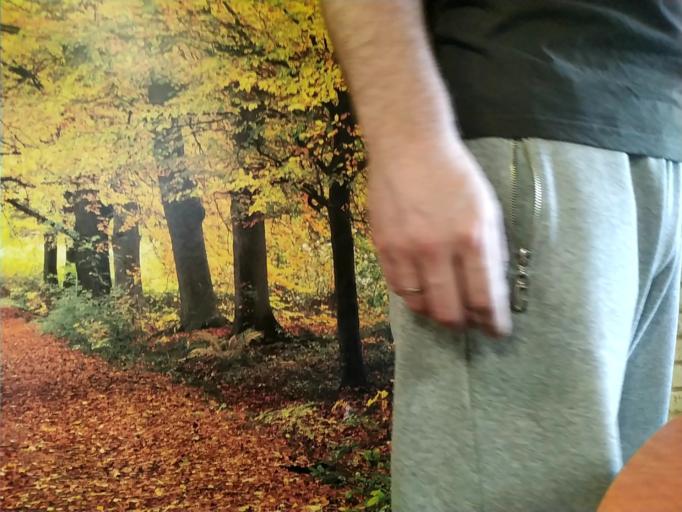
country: RU
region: Arkhangelskaya
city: Kargopol'
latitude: 60.9057
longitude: 38.8829
